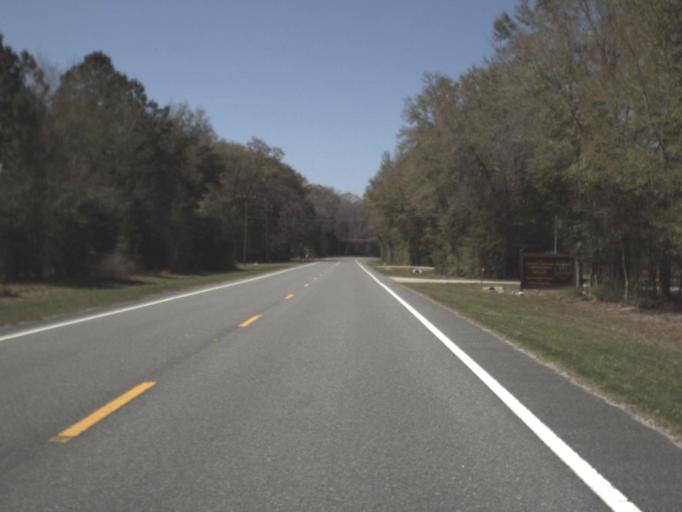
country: US
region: Florida
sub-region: Leon County
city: Woodville
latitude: 30.2382
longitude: -84.2628
